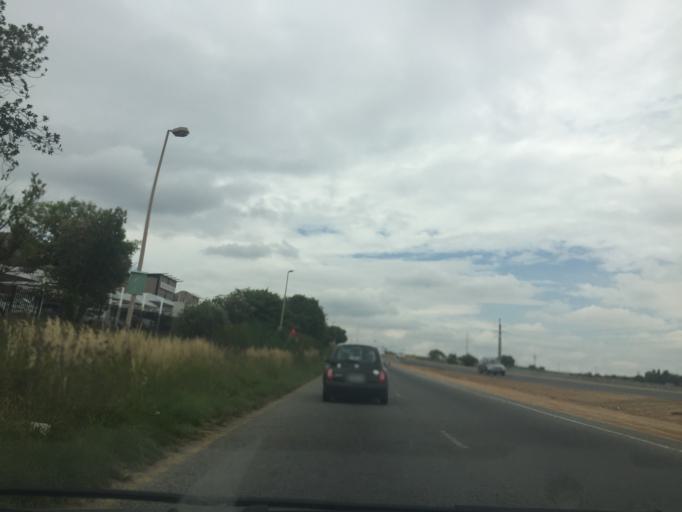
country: ZA
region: Gauteng
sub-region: City of Johannesburg Metropolitan Municipality
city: Midrand
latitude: -26.0127
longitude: 28.1296
